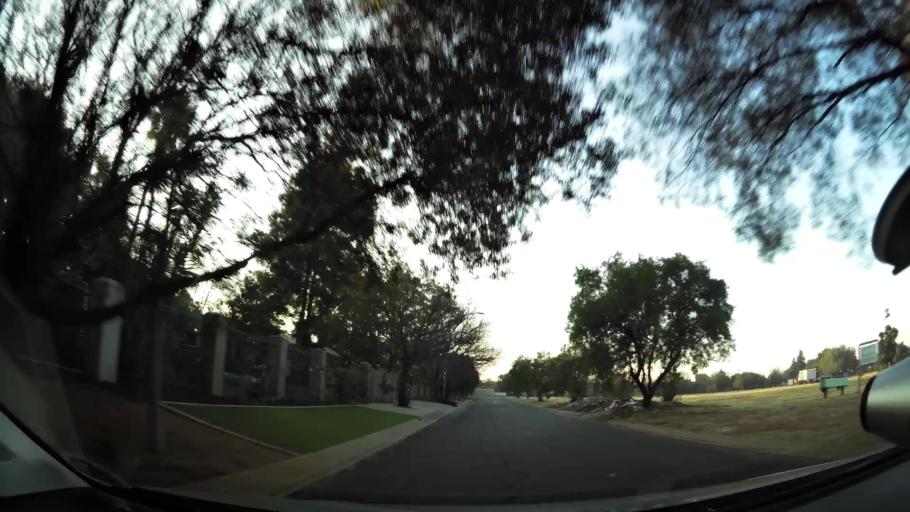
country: ZA
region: Orange Free State
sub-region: Mangaung Metropolitan Municipality
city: Bloemfontein
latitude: -29.1029
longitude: 26.1609
